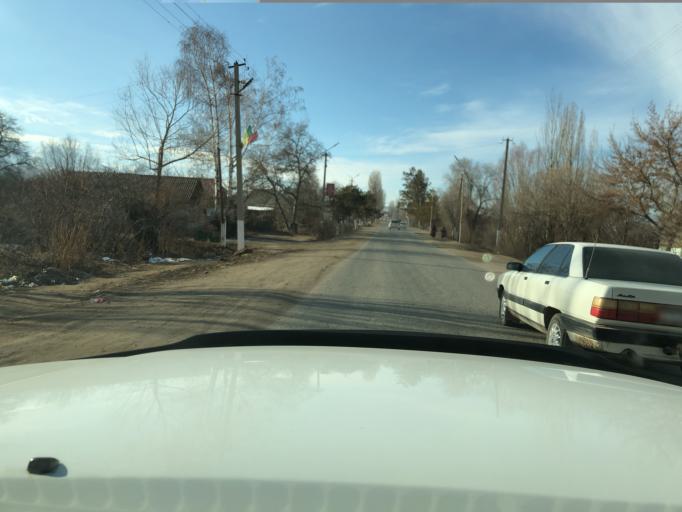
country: KG
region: Ysyk-Koel
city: Pokrovka
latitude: 42.3389
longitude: 77.9975
